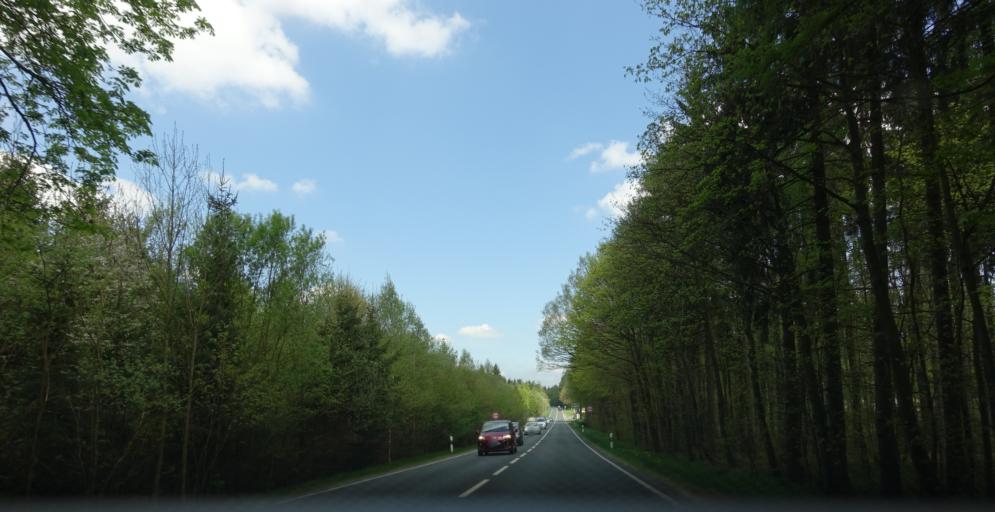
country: DE
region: Saxony
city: Grosshartmannsdorf
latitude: 50.8272
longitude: 13.3257
